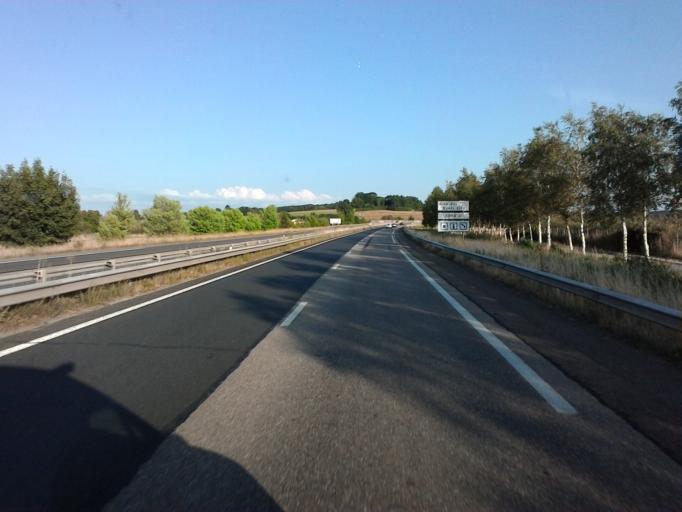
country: FR
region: Lorraine
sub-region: Departement des Vosges
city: Dogneville
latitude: 48.2221
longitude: 6.4495
